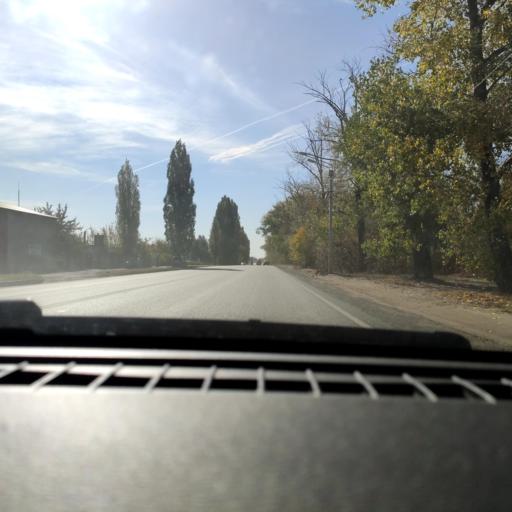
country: RU
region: Voronezj
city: Maslovka
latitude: 51.5966
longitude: 39.2518
